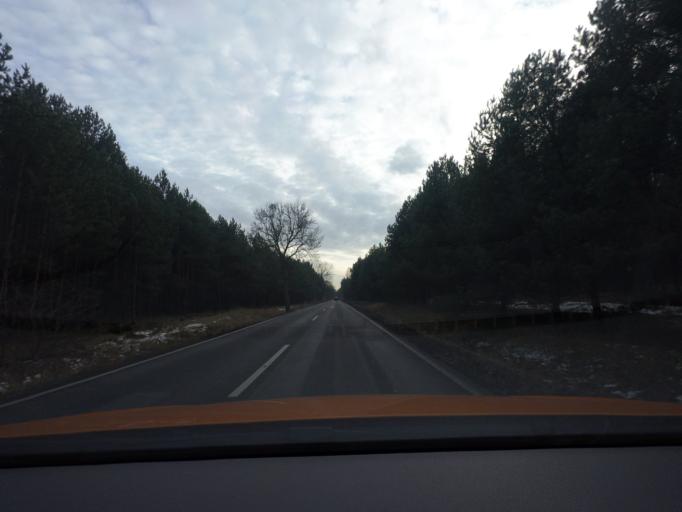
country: DE
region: Brandenburg
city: Glienicke
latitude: 52.7079
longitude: 13.3662
